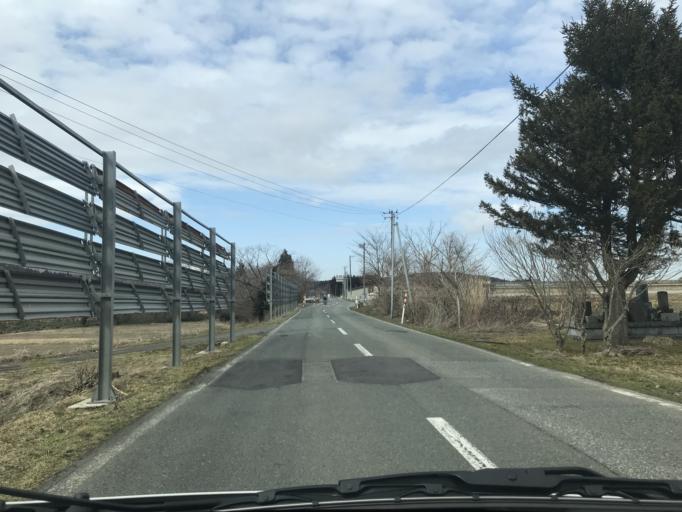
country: JP
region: Iwate
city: Hanamaki
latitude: 39.3420
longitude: 140.9821
